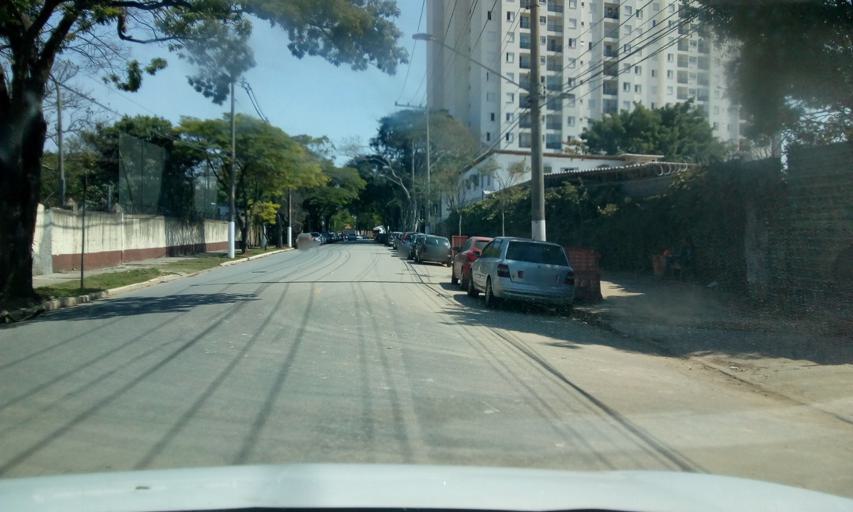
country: BR
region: Sao Paulo
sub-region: Osasco
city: Osasco
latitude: -23.5182
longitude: -46.7140
